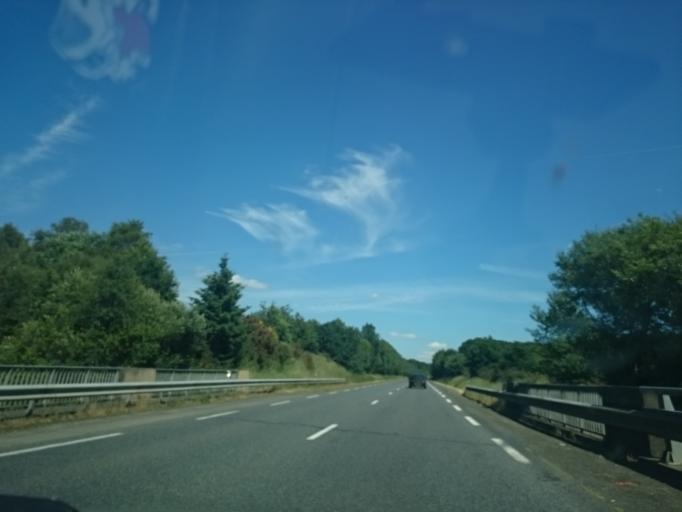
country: FR
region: Brittany
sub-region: Departement des Cotes-d'Armor
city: Plouguernevel
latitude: 48.2446
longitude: -3.2453
